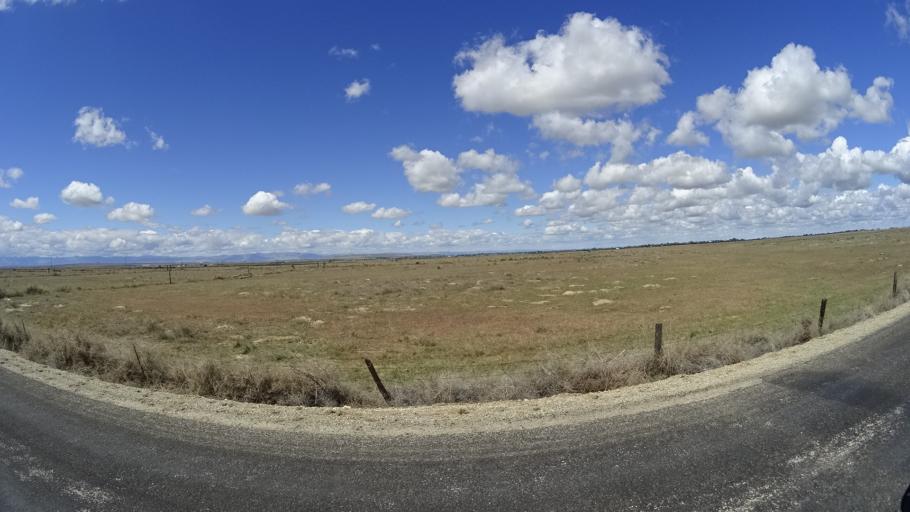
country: US
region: Idaho
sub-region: Ada County
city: Kuna
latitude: 43.4620
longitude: -116.2744
